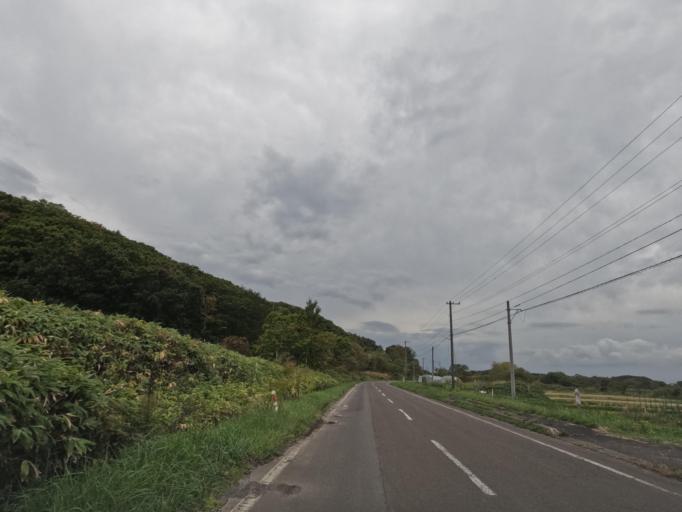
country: JP
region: Hokkaido
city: Date
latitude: 42.3975
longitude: 140.9192
